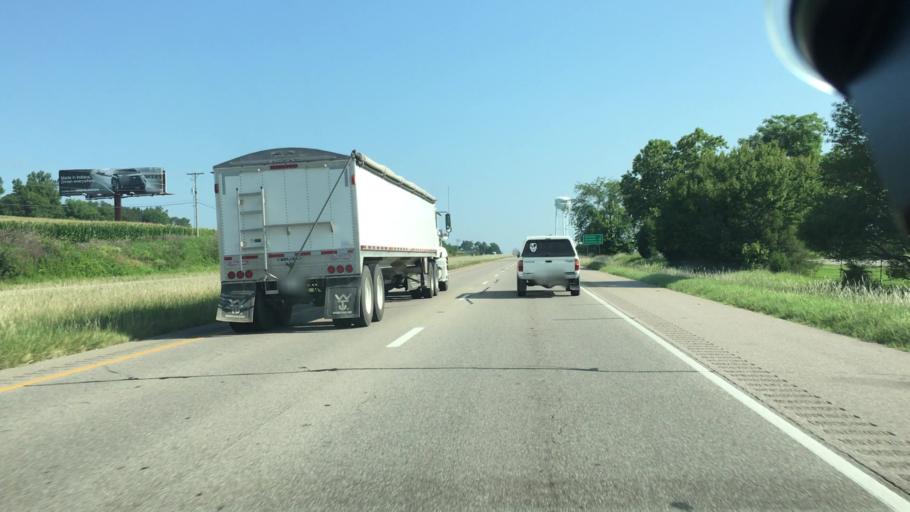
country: US
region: Indiana
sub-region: Gibson County
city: Fort Branch
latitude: 38.2836
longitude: -87.5675
